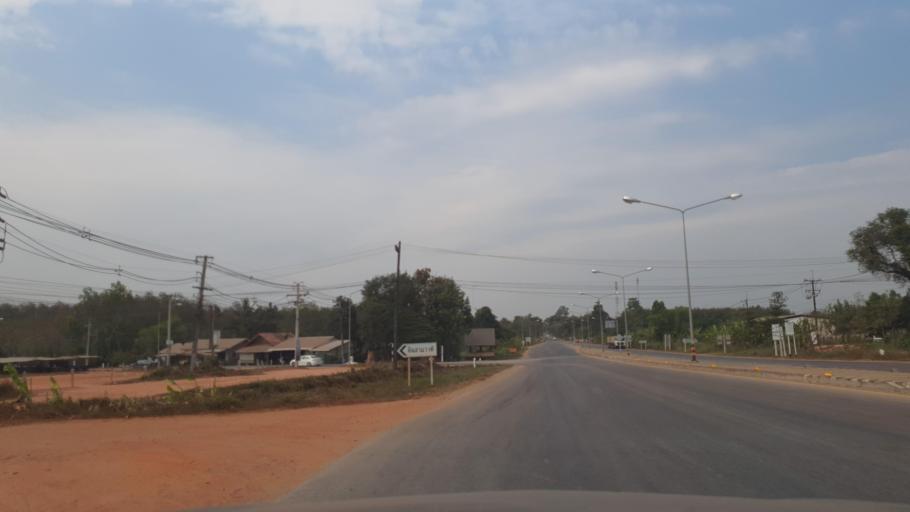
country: TH
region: Changwat Bueng Kan
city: Si Wilai
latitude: 18.3053
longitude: 103.8115
